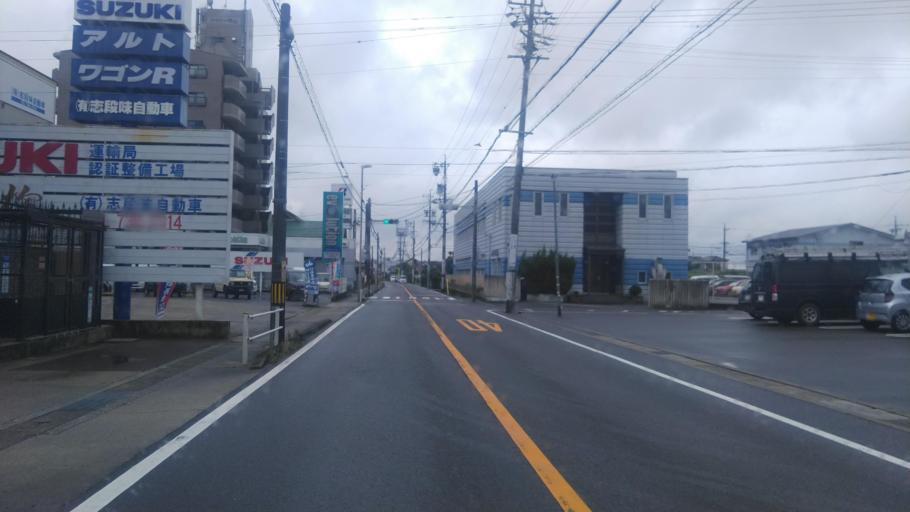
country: JP
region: Aichi
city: Kasugai
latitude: 35.2456
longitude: 137.0295
